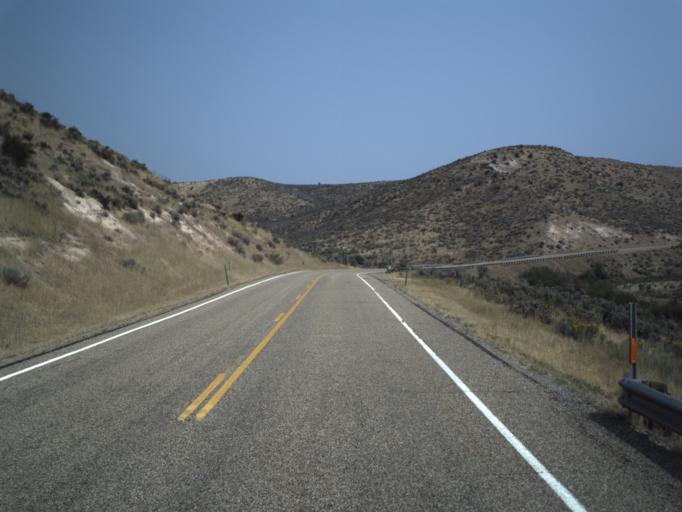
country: US
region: Utah
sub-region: Morgan County
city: Morgan
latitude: 40.9335
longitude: -111.5683
